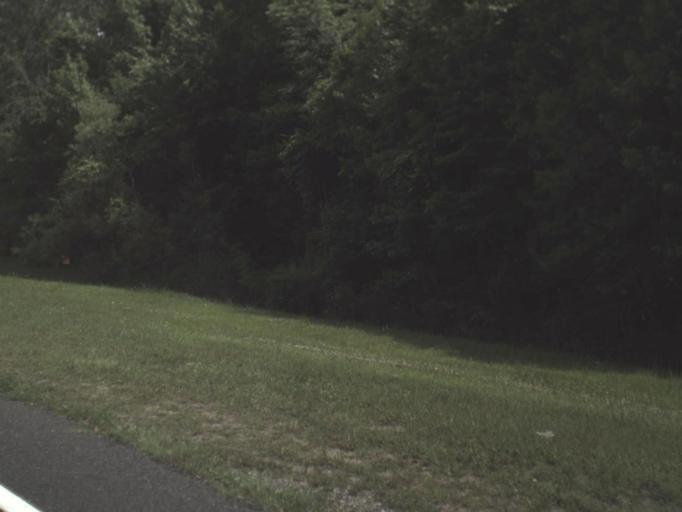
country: US
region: Florida
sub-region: Saint Johns County
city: Fruit Cove
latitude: 30.1888
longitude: -81.5516
